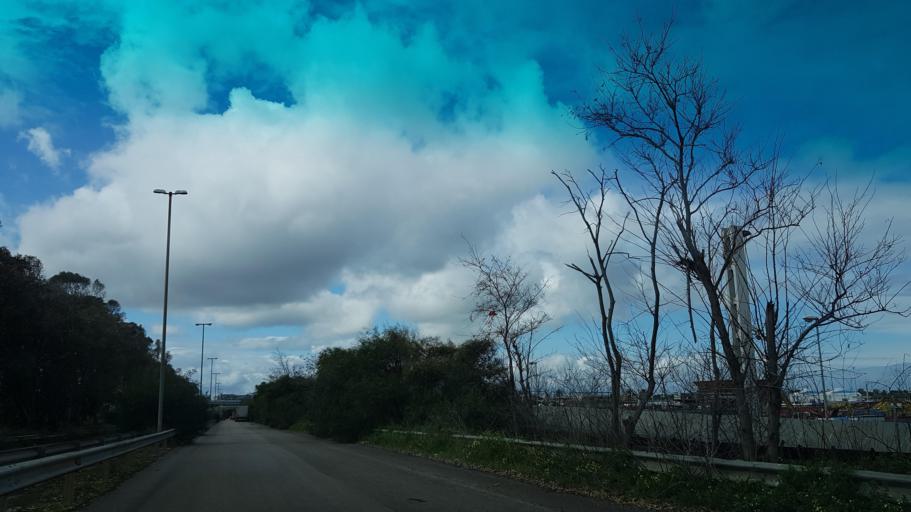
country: IT
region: Apulia
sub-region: Provincia di Brindisi
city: Materdomini
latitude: 40.6432
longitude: 17.9677
